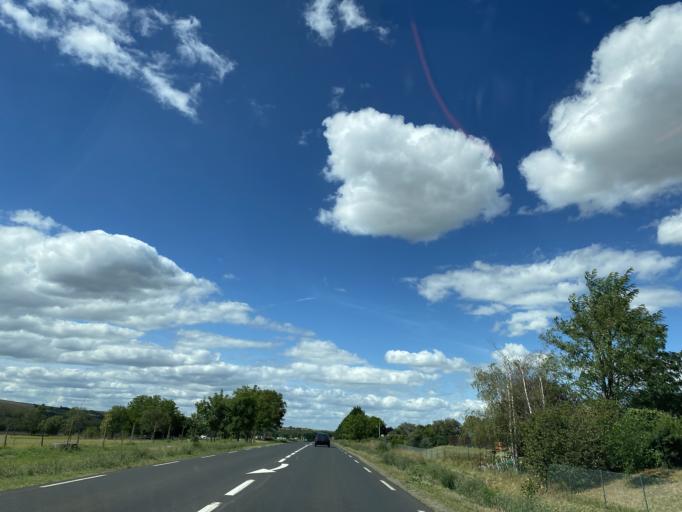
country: FR
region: Auvergne
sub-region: Departement du Puy-de-Dome
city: Mezel
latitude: 45.7521
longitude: 3.2373
